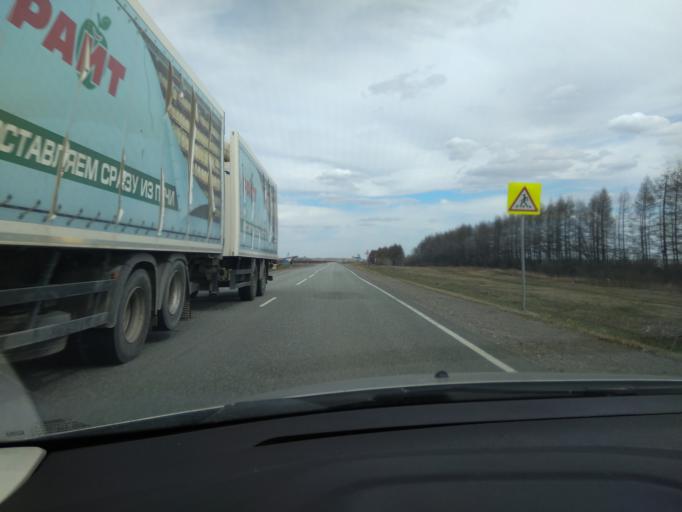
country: RU
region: Sverdlovsk
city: Yelanskiy
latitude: 56.7739
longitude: 62.4553
